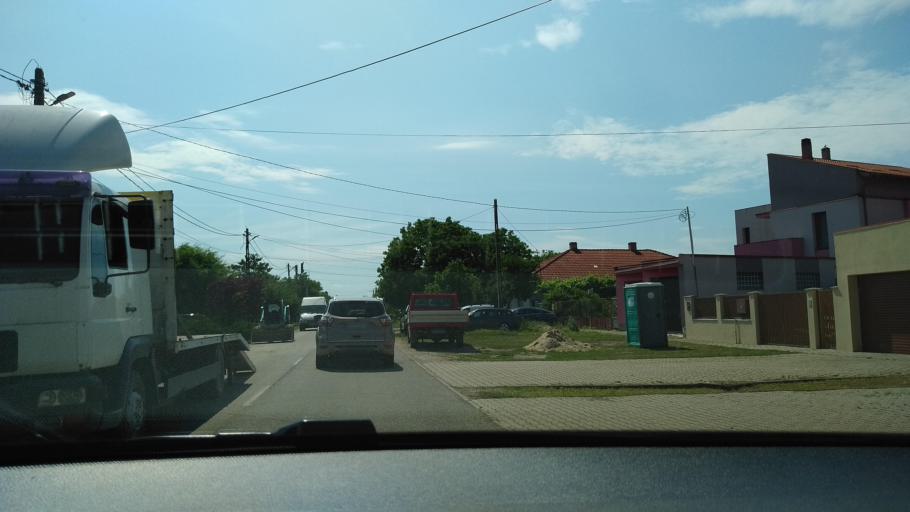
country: RO
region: Timis
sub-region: Comuna Dumbravita
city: Dumbravita
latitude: 45.8000
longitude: 21.2412
